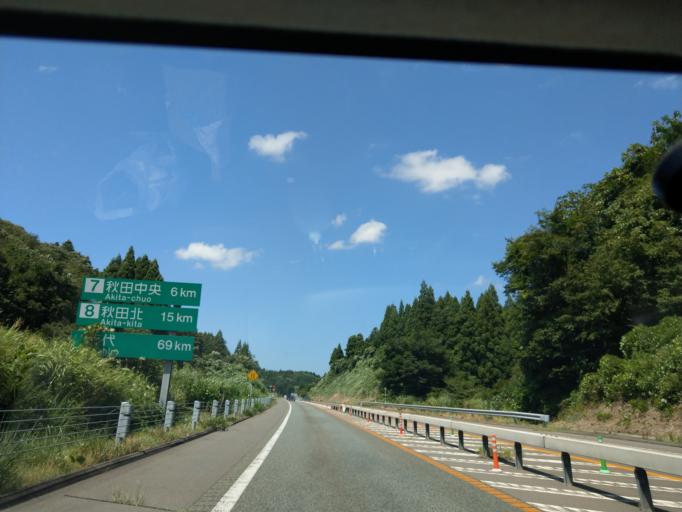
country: JP
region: Akita
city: Akita
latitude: 39.6714
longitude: 140.1878
